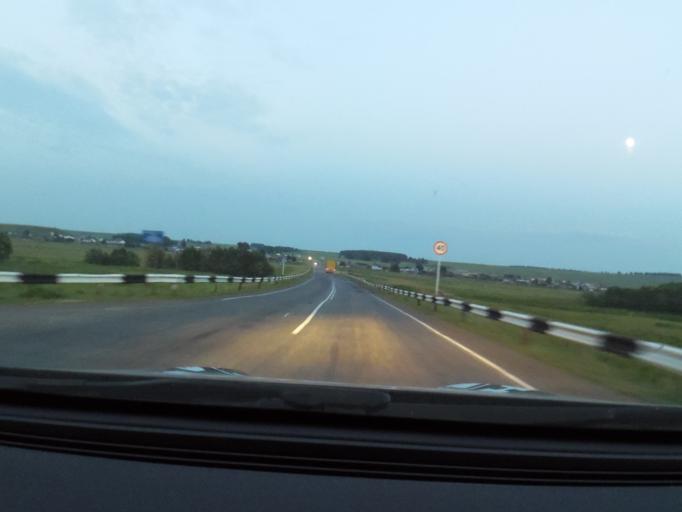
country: RU
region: Sverdlovsk
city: Sarana
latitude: 56.1325
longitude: 58.0075
